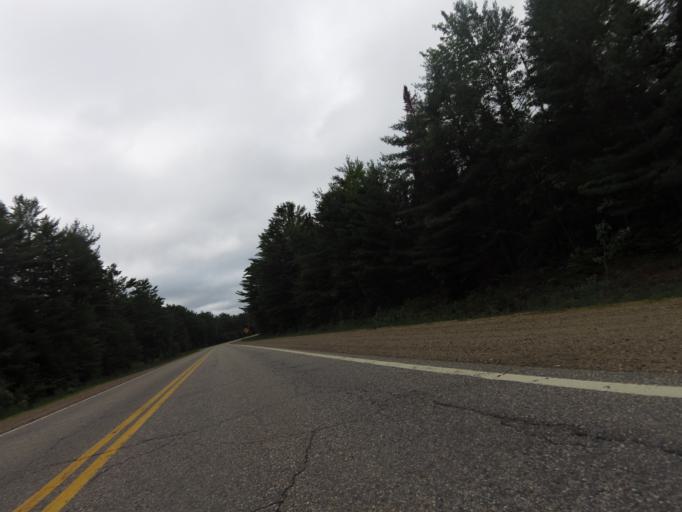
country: CA
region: Quebec
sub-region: Outaouais
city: Shawville
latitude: 45.8603
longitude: -76.4100
